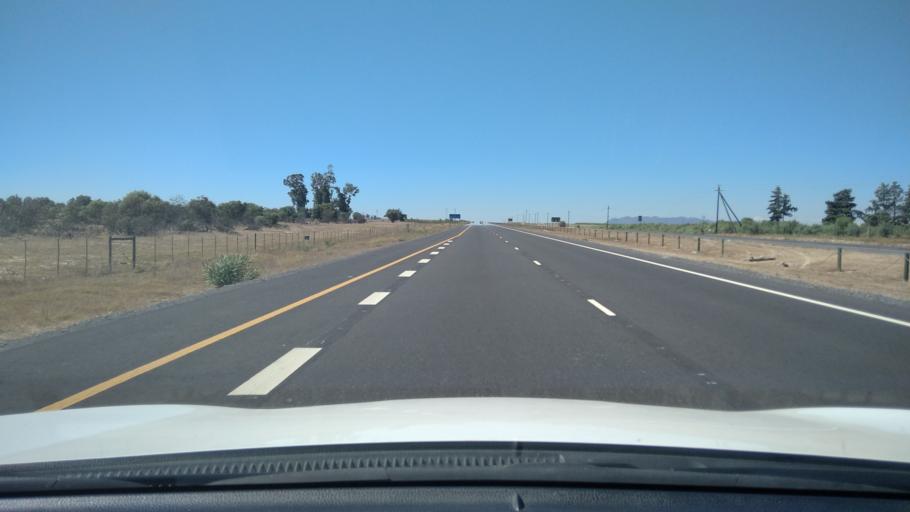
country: ZA
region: Western Cape
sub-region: West Coast District Municipality
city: Malmesbury
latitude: -33.5604
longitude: 18.6261
